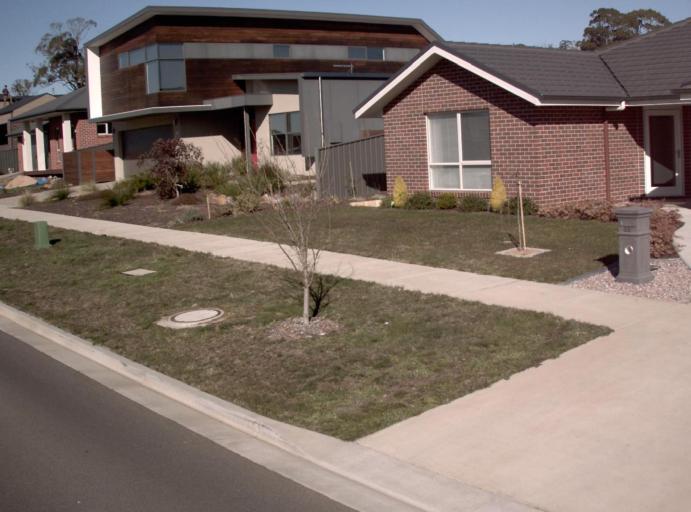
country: AU
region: Tasmania
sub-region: Launceston
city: Summerhill
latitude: -41.4750
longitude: 147.1498
